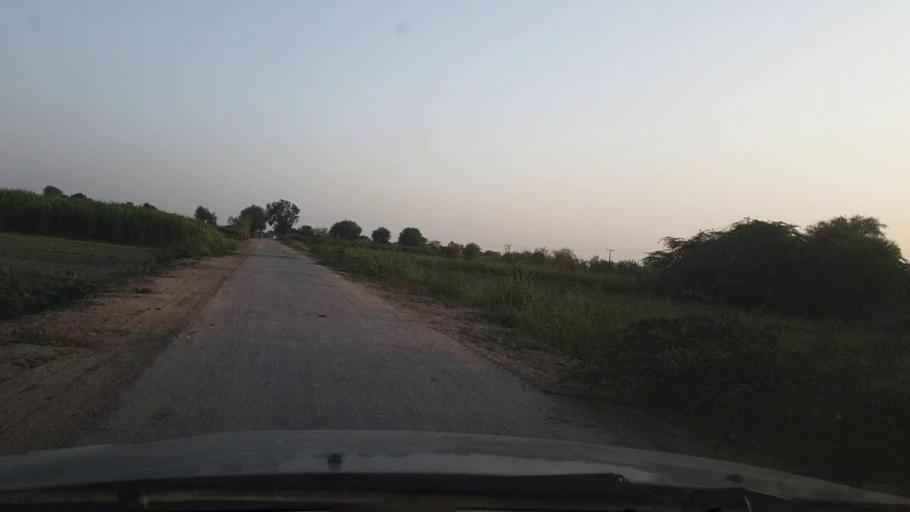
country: PK
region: Sindh
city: Tando Ghulam Ali
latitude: 25.1535
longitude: 68.9757
